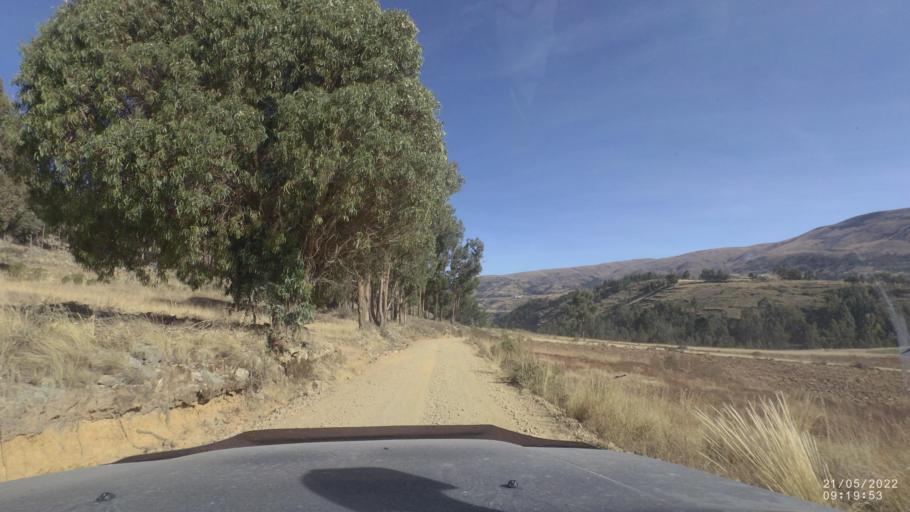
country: BO
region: Cochabamba
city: Cochabamba
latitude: -17.3575
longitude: -66.0224
